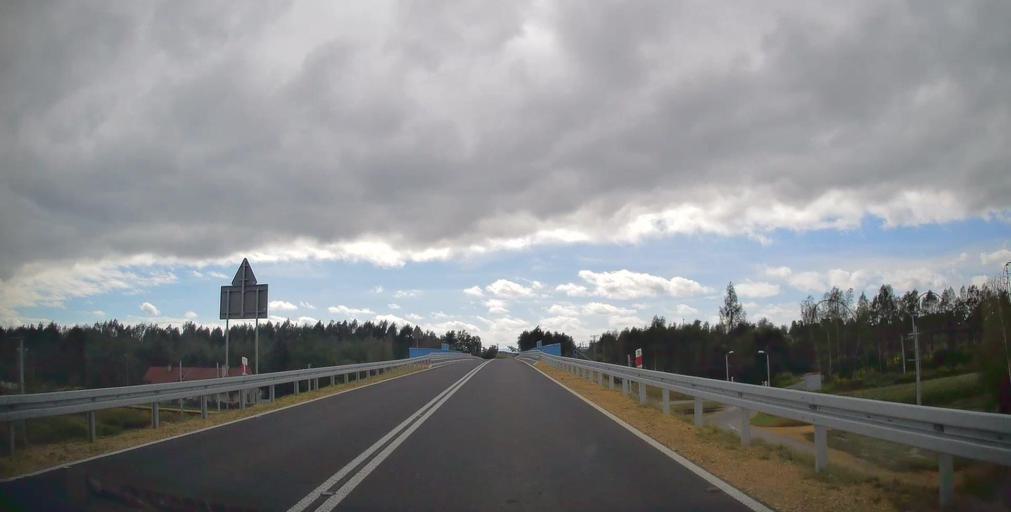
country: PL
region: Lesser Poland Voivodeship
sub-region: Powiat oswiecimski
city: Zator
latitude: 50.0039
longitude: 19.4229
